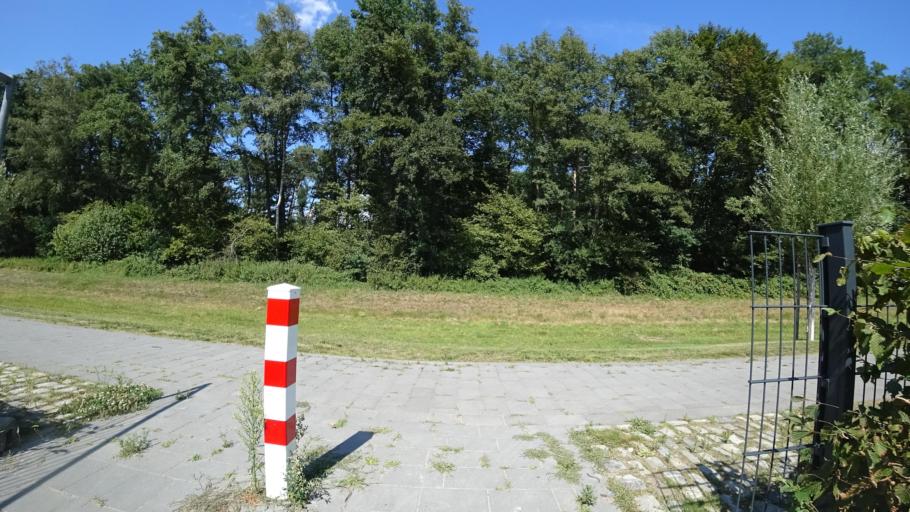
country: DE
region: North Rhine-Westphalia
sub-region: Regierungsbezirk Detmold
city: Guetersloh
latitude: 51.9301
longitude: 8.3932
